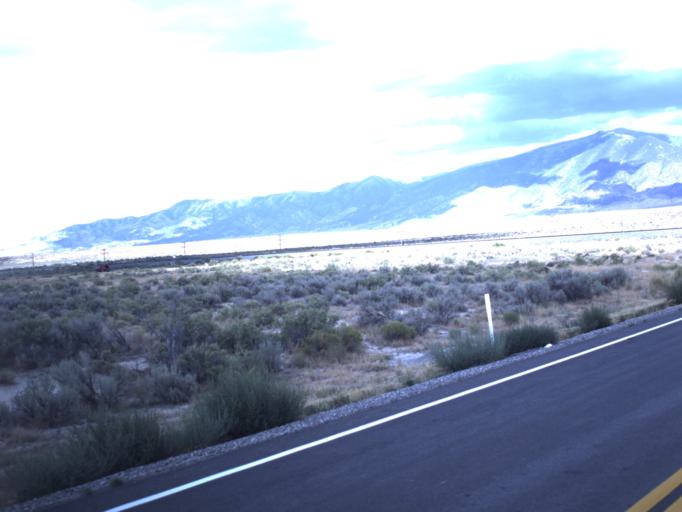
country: US
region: Utah
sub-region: Tooele County
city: Tooele
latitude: 40.3370
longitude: -112.4110
